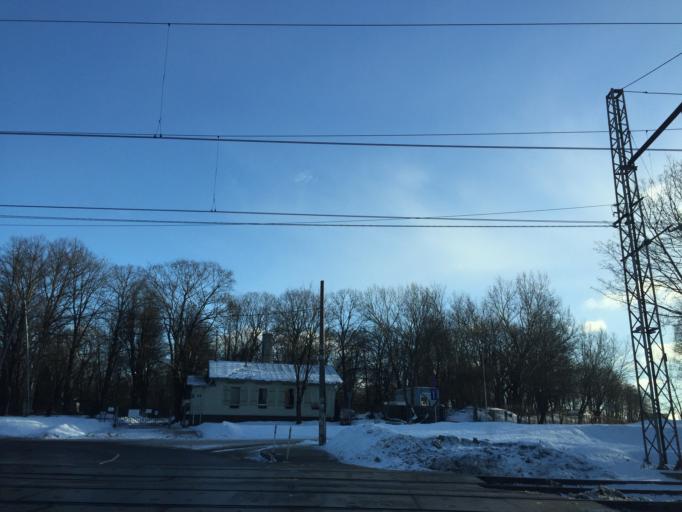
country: LV
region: Riga
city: Riga
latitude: 56.9473
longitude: 24.1542
